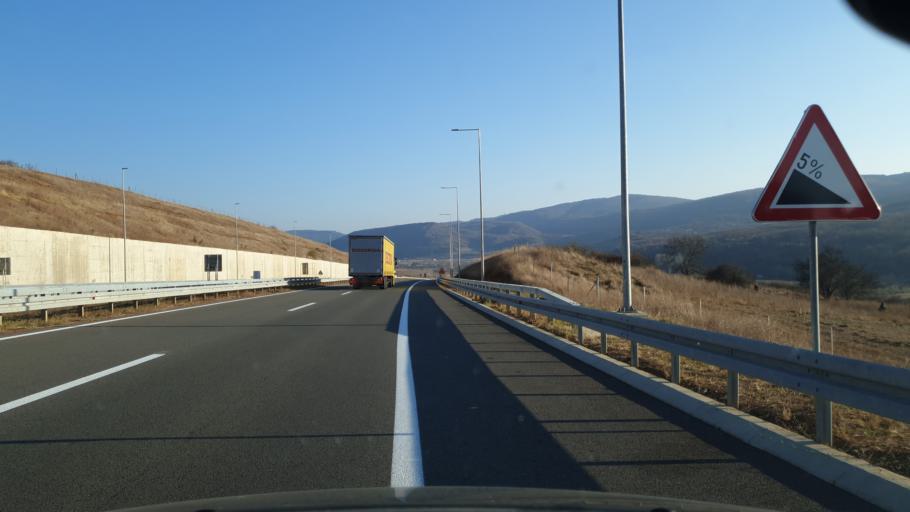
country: RS
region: Central Serbia
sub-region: Pirotski Okrug
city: Dimitrovgrad
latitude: 43.0227
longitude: 22.7946
